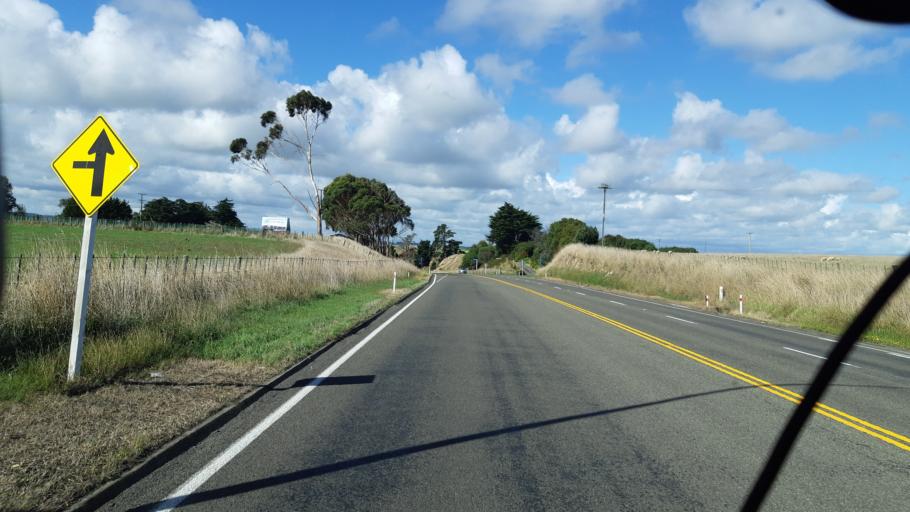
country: NZ
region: Manawatu-Wanganui
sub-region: Wanganui District
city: Wanganui
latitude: -40.0277
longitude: 175.1941
